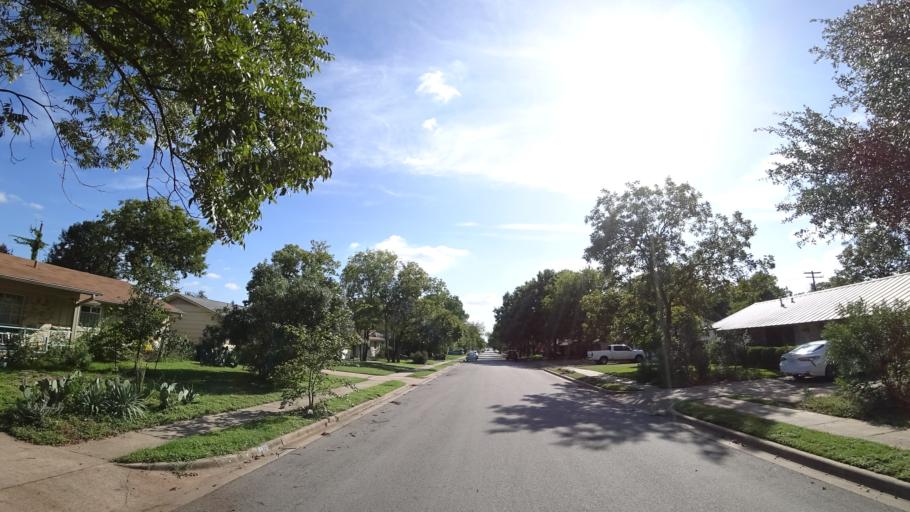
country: US
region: Texas
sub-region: Williamson County
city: Jollyville
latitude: 30.3676
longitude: -97.7311
